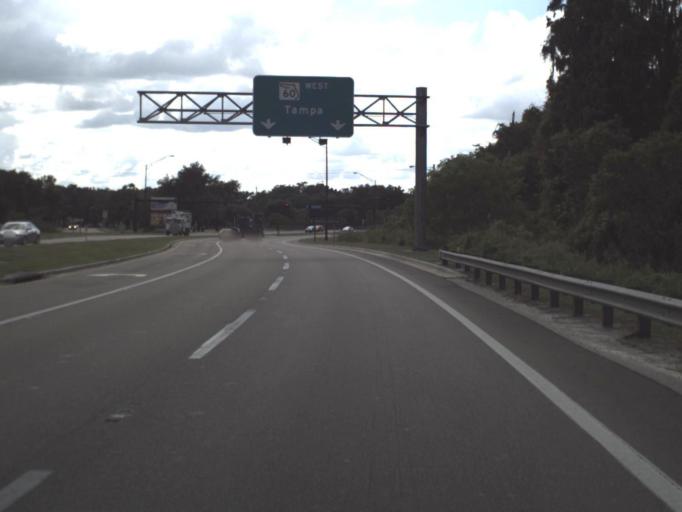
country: US
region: Florida
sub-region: Polk County
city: Bartow
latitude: 27.9020
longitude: -81.8189
